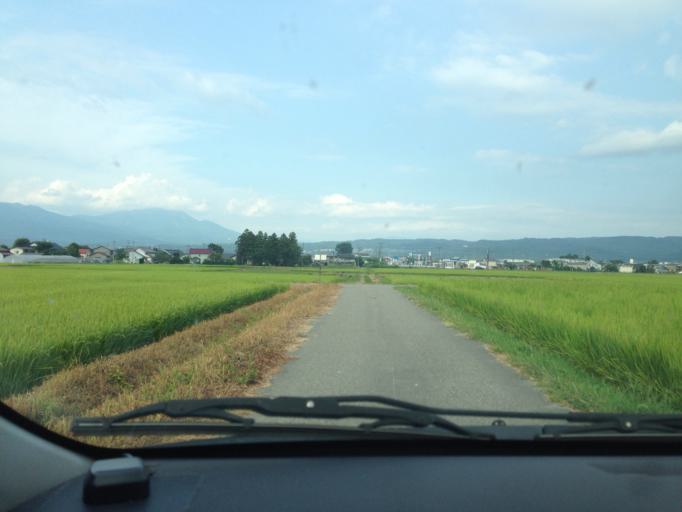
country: JP
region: Fukushima
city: Kitakata
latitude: 37.5148
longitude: 139.8968
